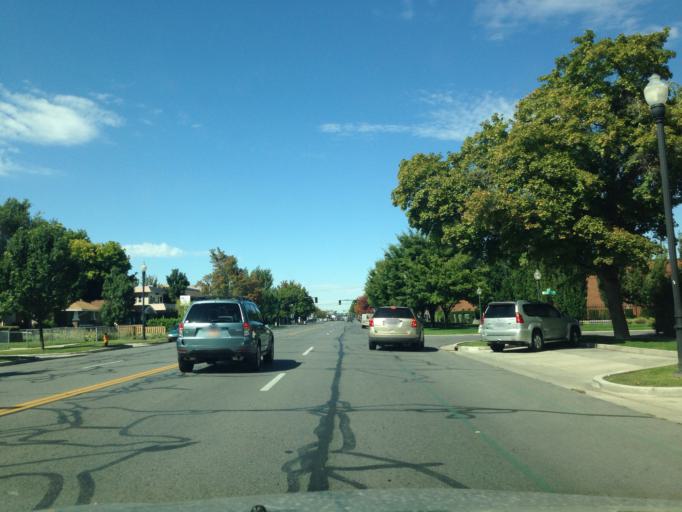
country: US
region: Utah
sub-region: Salt Lake County
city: Salt Lake City
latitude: 40.7498
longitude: -111.8834
